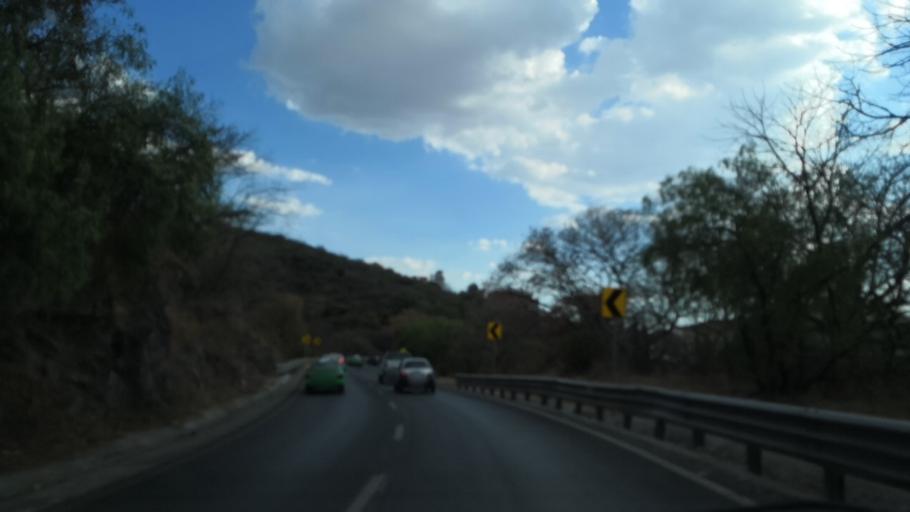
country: MX
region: Guanajuato
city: Marfil
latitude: 20.9999
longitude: -101.2847
